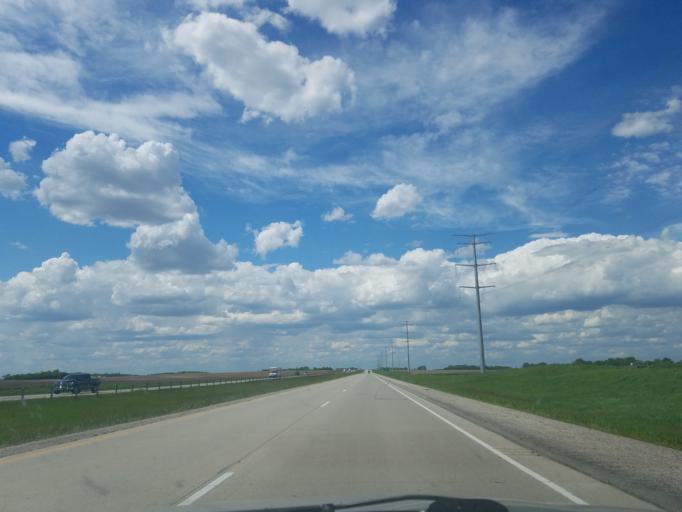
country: US
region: Minnesota
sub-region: Clay County
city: Barnesville
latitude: 46.5372
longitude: -96.3008
